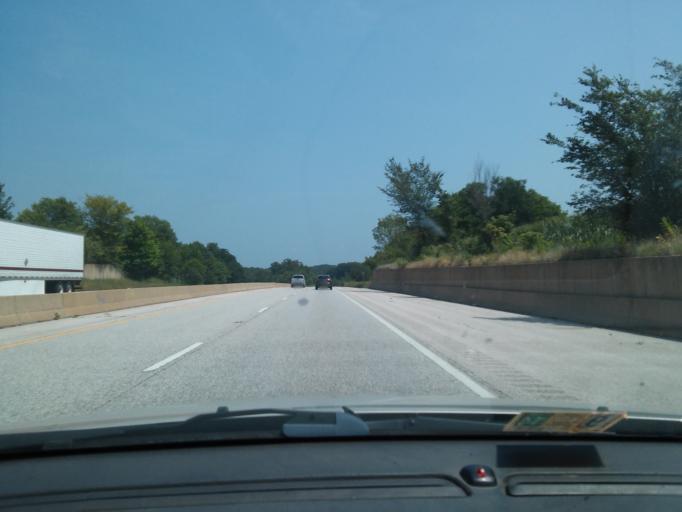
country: US
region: Illinois
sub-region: Pike County
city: Griggsville
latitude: 39.6811
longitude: -90.6674
